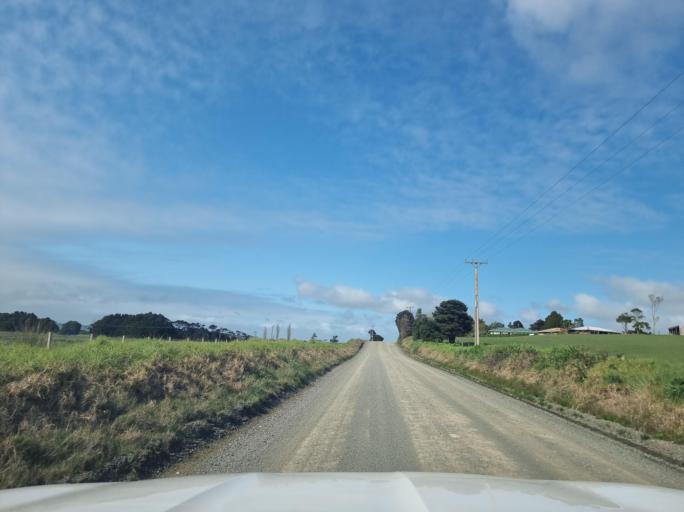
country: NZ
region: Auckland
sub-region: Auckland
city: Wellsford
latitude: -36.1089
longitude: 174.5009
